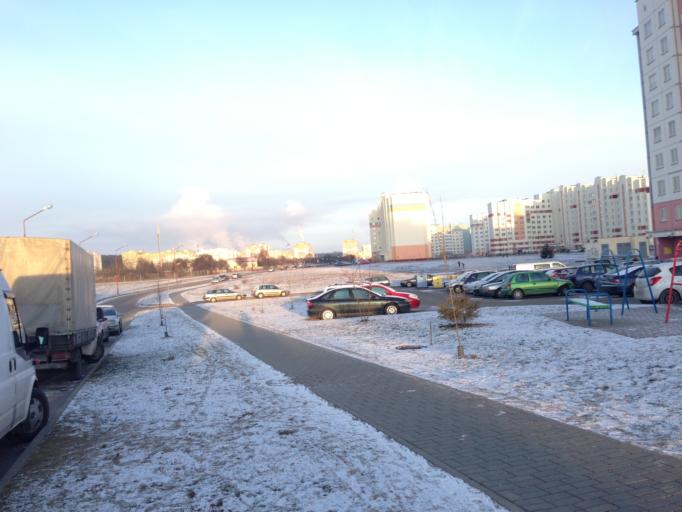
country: BY
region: Grodnenskaya
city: Hrodna
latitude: 53.6372
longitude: 23.8523
